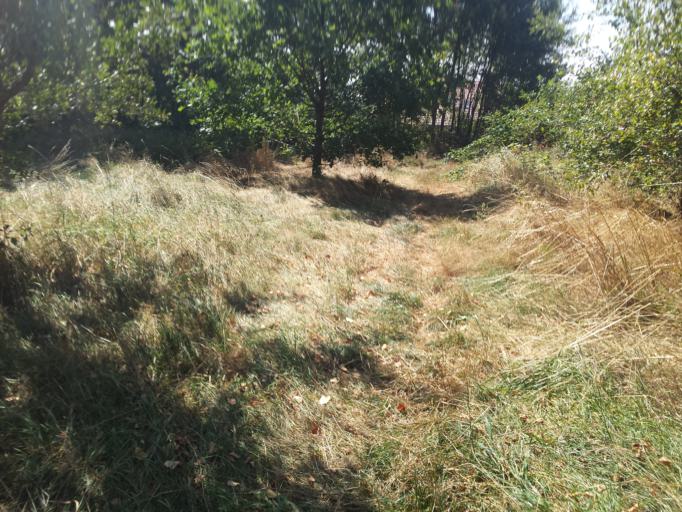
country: PL
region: Swietokrzyskie
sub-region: Powiat kielecki
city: Daleszyce
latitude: 50.8015
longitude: 20.7691
